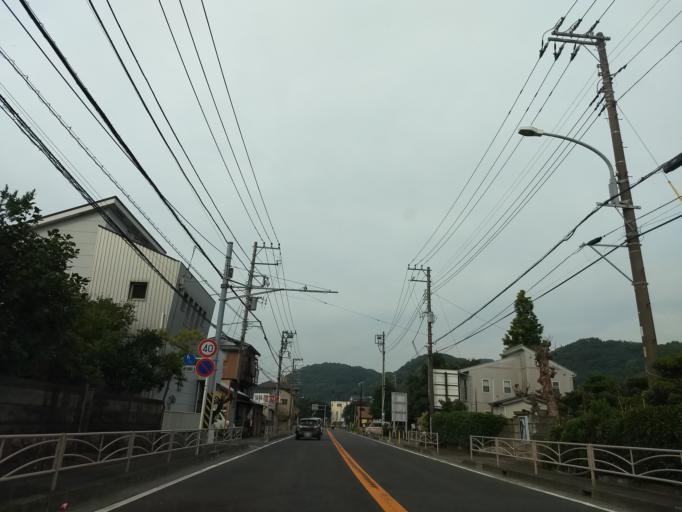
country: JP
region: Kanagawa
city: Hiratsuka
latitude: 35.3205
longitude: 139.3254
